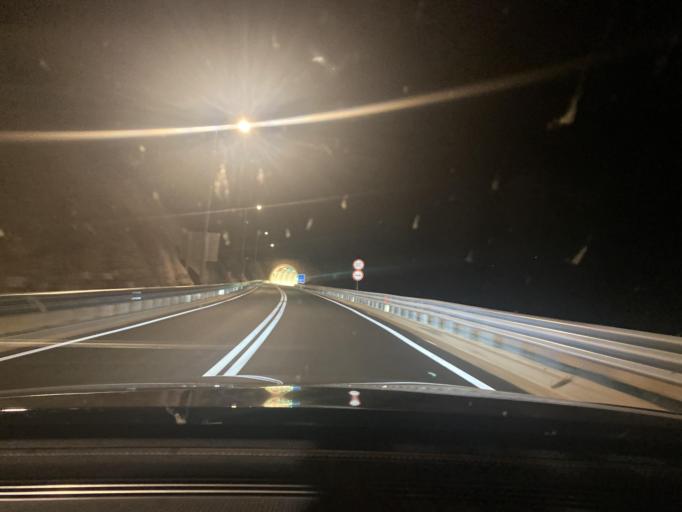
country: BA
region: Federation of Bosnia and Herzegovina
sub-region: Hercegovacko-Bosanski Kanton
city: Neum
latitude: 42.9039
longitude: 17.5432
